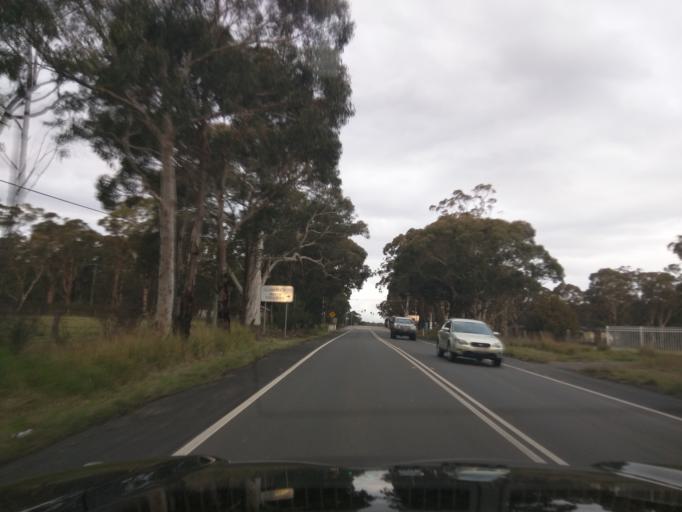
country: AU
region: New South Wales
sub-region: Wollondilly
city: Douglas Park
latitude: -34.2055
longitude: 150.7918
